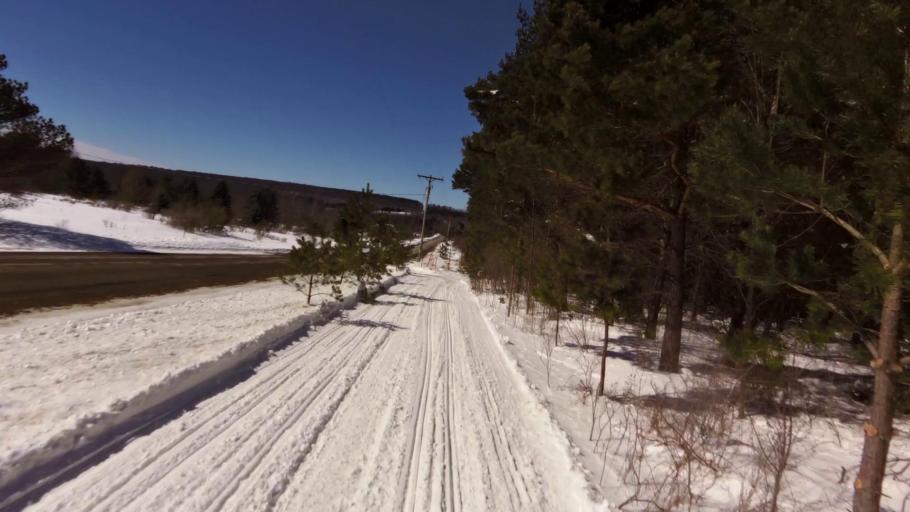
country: US
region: New York
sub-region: Allegany County
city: Houghton
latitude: 42.4112
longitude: -78.2949
